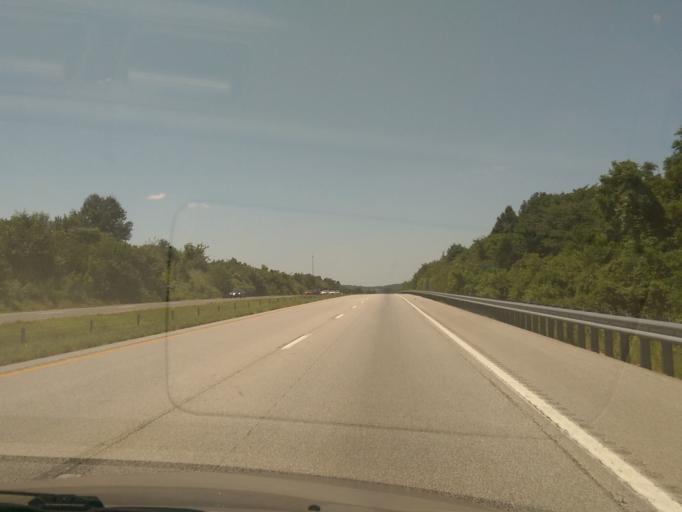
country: US
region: Missouri
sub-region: Cooper County
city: Boonville
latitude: 38.9336
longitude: -92.9658
